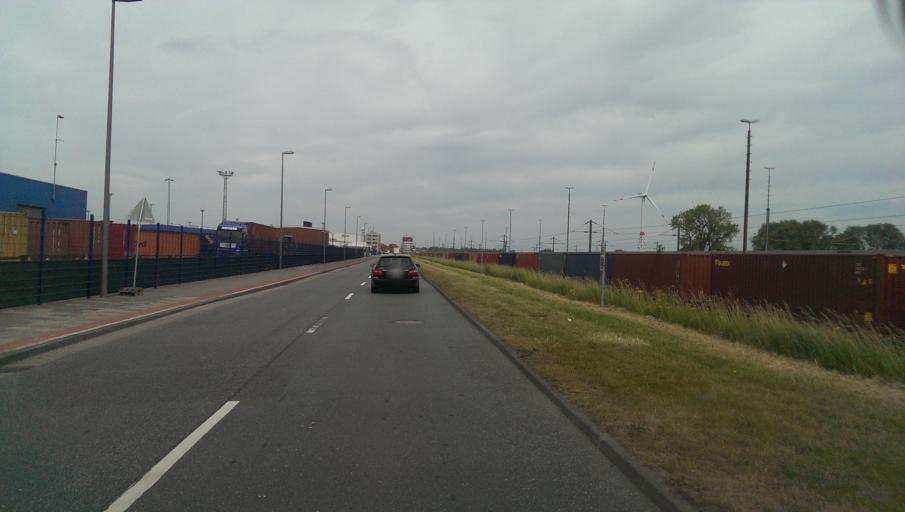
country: DE
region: Bremen
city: Bremerhaven
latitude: 53.5856
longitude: 8.5445
